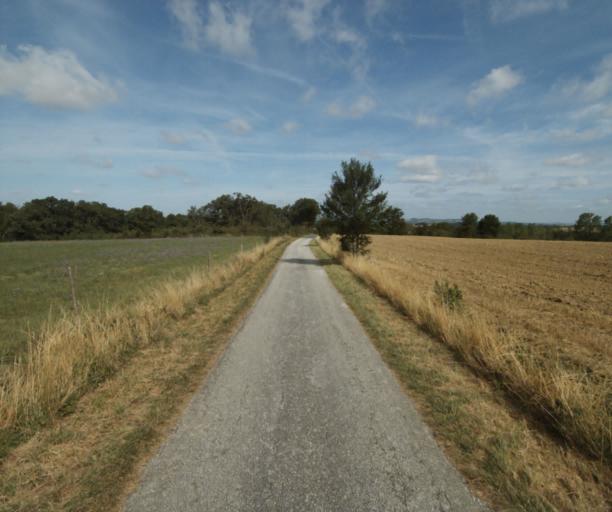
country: FR
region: Midi-Pyrenees
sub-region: Departement du Tarn
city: Soreze
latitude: 43.4760
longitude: 2.0974
